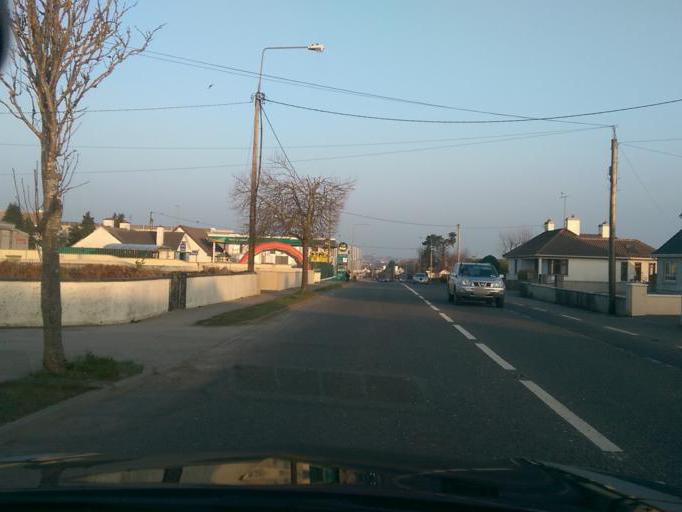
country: IE
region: Connaught
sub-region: County Galway
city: Loughrea
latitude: 53.2019
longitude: -8.5858
